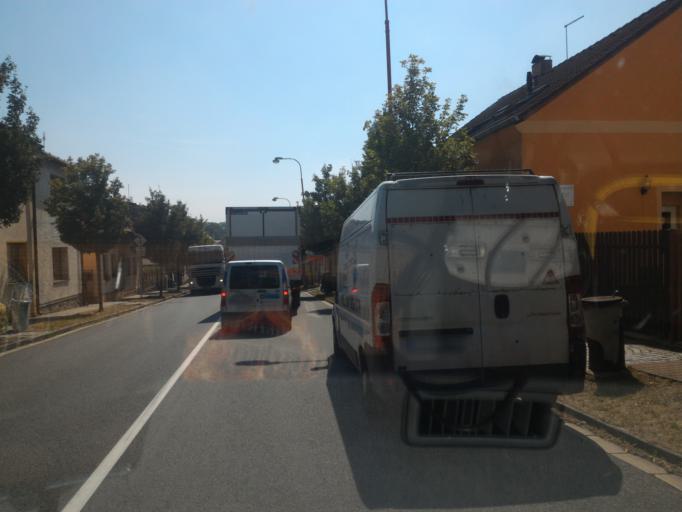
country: CZ
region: Pardubicky
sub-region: Okres Chrudim
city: Hlinsko
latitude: 49.7630
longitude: 15.8983
